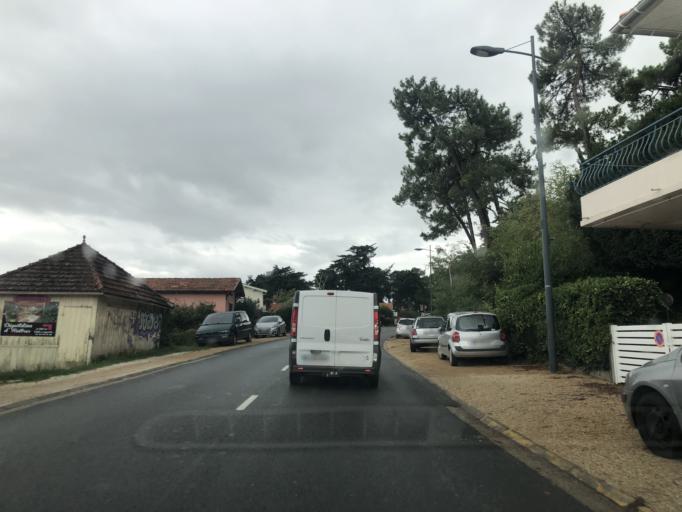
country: FR
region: Aquitaine
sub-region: Departement de la Gironde
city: Arcachon
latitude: 44.6996
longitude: -1.2298
